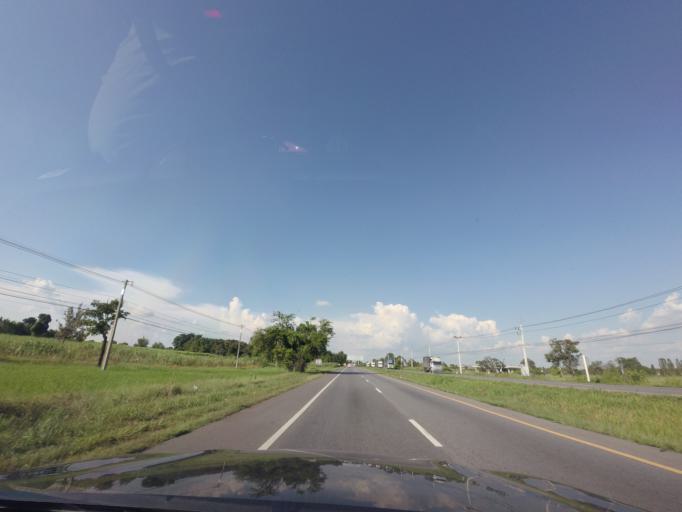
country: TH
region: Khon Kaen
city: Non Sila
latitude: 15.9557
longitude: 102.6862
